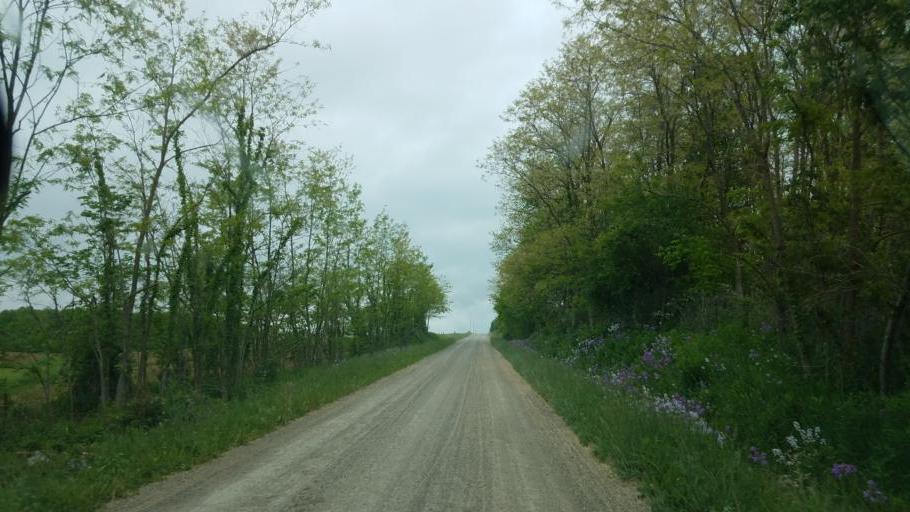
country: US
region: Ohio
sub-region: Knox County
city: Fredericktown
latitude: 40.5457
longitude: -82.6429
